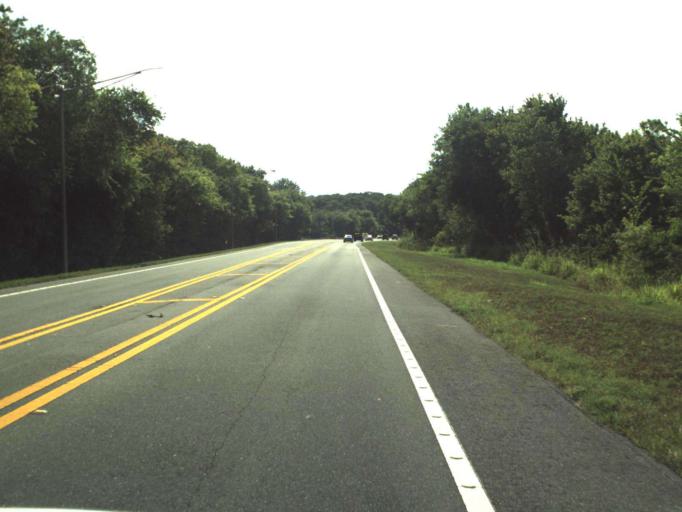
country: US
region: Florida
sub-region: Seminole County
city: Sanford
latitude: 28.8251
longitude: -81.3017
